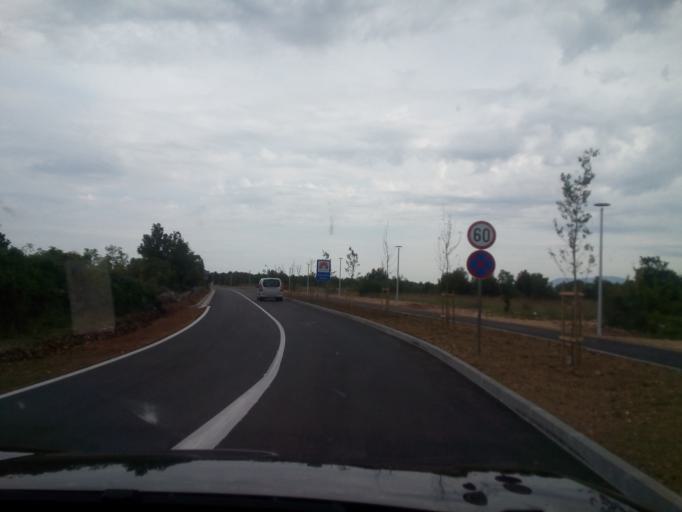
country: HR
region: Sibensko-Kniniska
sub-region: Grad Sibenik
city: Sibenik
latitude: 43.7846
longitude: 15.9666
